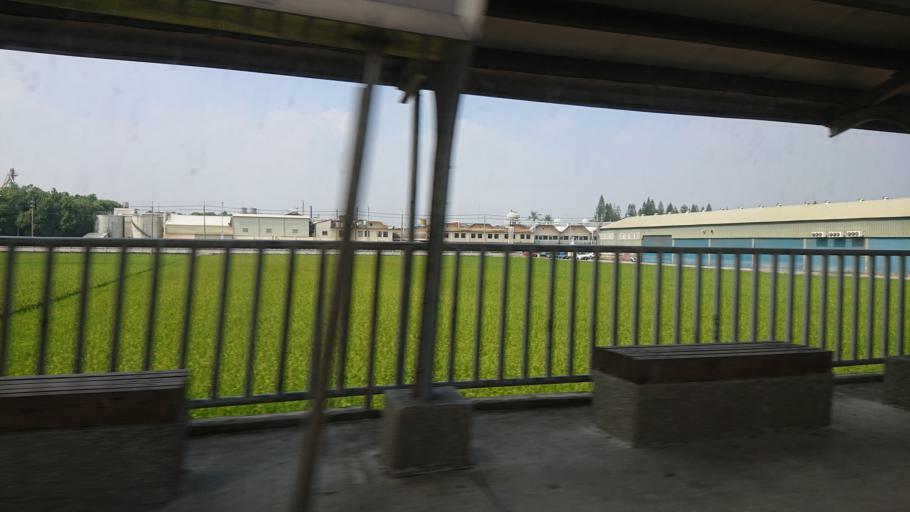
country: TW
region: Taiwan
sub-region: Yunlin
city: Douliu
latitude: 23.6396
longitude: 120.4709
